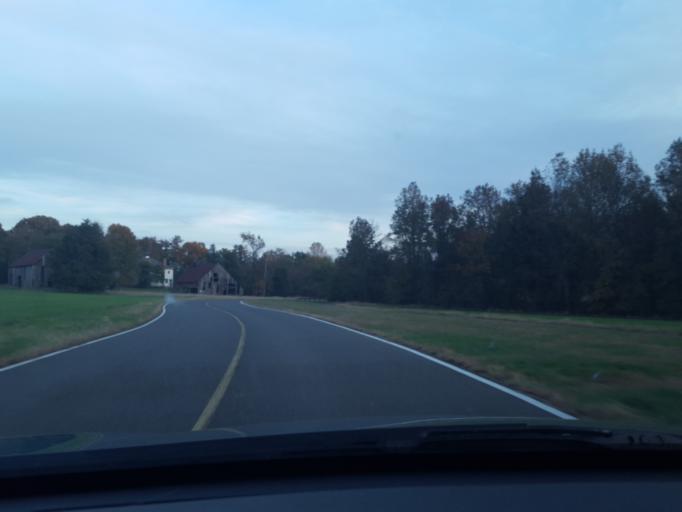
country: US
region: Maryland
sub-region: Prince George's County
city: Kettering
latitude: 38.8822
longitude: -76.7884
